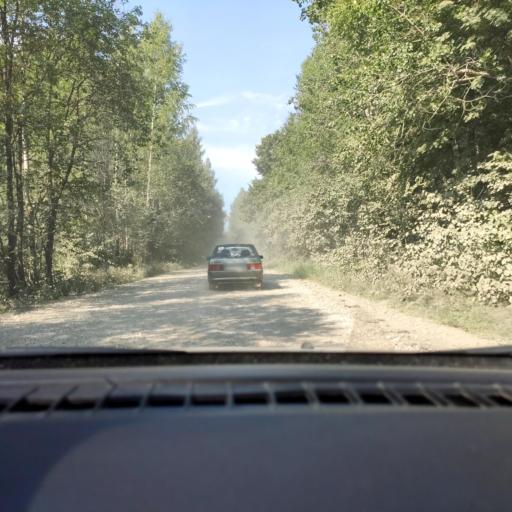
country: RU
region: Perm
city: Polazna
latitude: 58.1250
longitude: 56.4364
